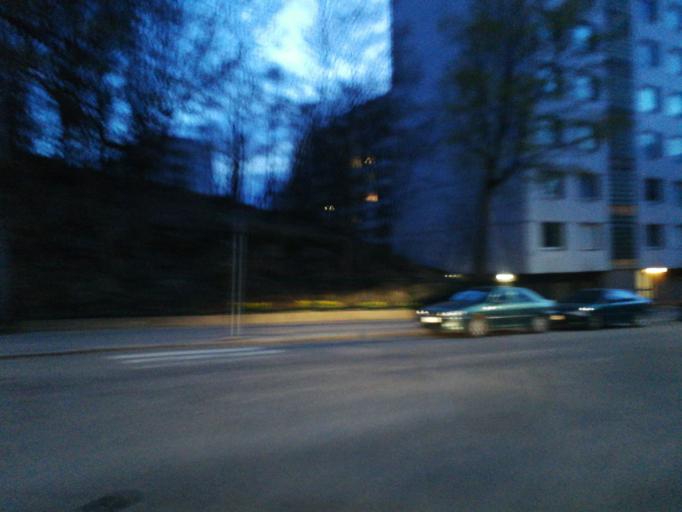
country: FI
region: Varsinais-Suomi
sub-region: Turku
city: Turku
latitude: 60.4424
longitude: 22.2557
